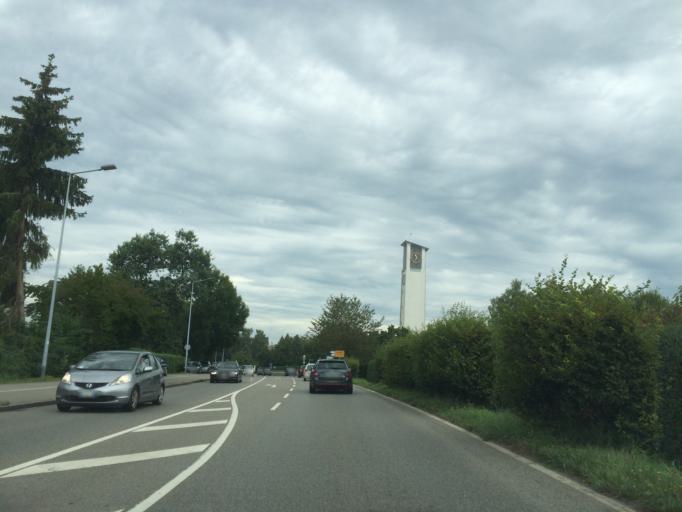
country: DE
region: Baden-Wuerttemberg
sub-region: Tuebingen Region
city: Friedrichshafen
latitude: 47.6677
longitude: 9.4233
